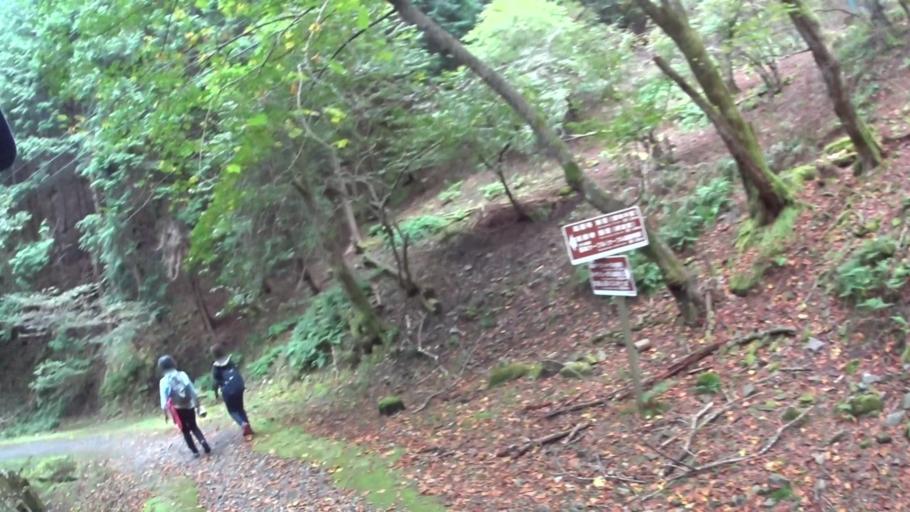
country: JP
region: Shiga Prefecture
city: Otsu-shi
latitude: 35.0670
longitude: 135.8323
